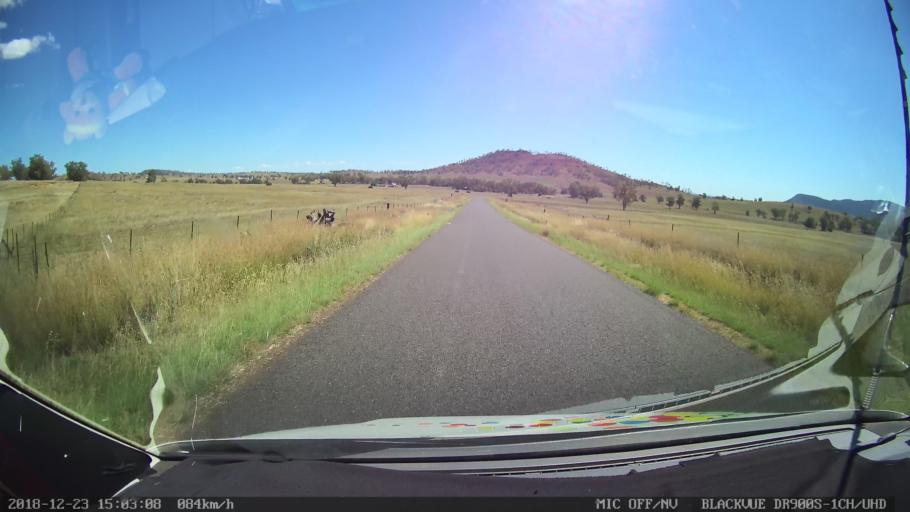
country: AU
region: New South Wales
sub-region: Tamworth Municipality
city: Manilla
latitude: -30.7356
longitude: 150.7680
